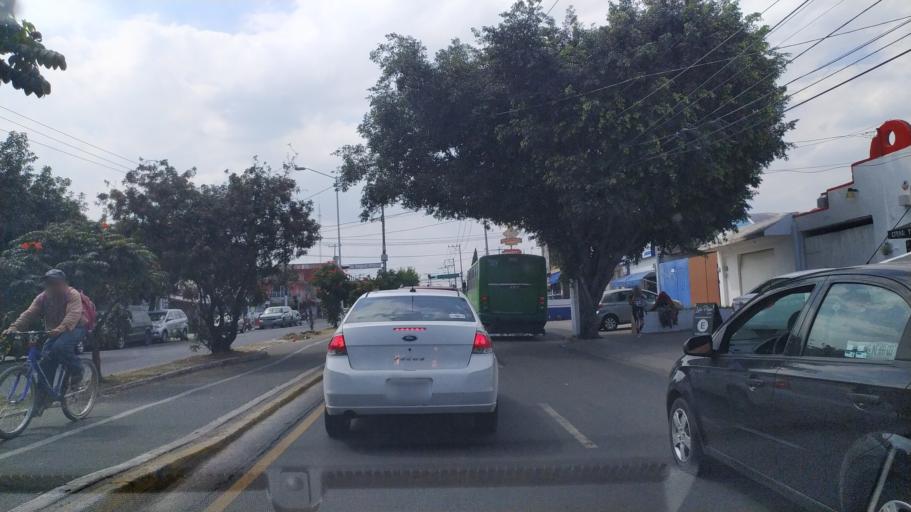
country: MX
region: Jalisco
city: Zapopan2
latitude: 20.7303
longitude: -103.4216
